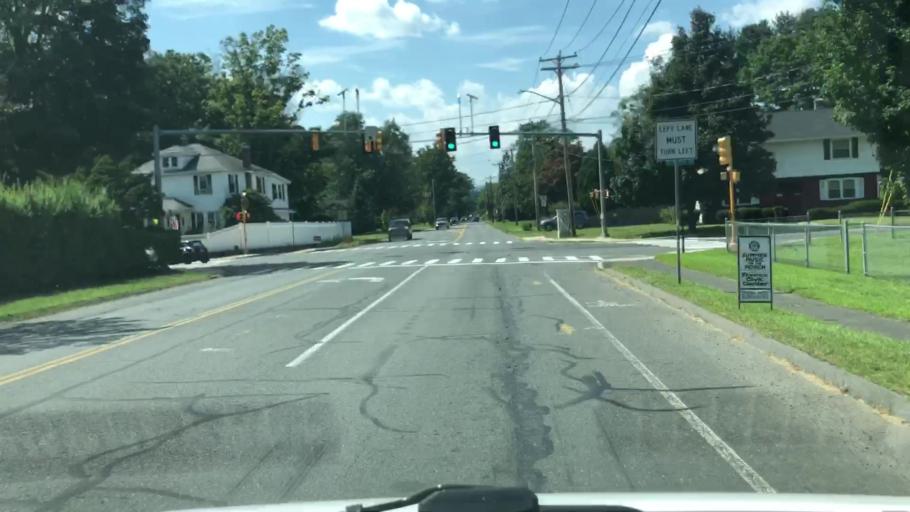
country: US
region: Massachusetts
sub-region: Hampshire County
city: Northampton
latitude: 42.3445
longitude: -72.6709
